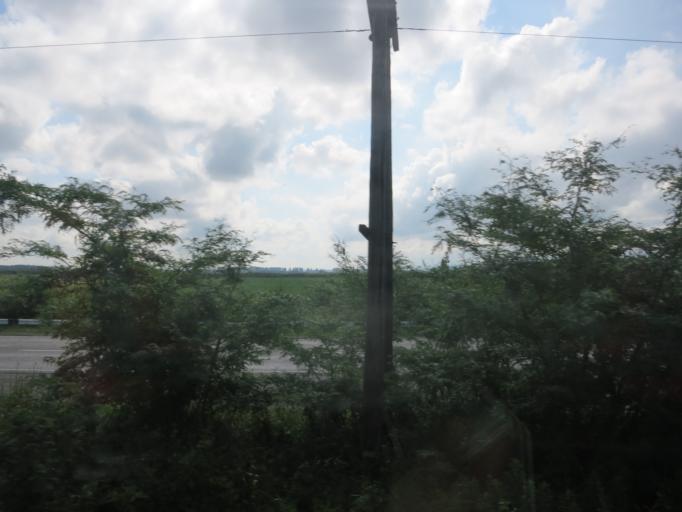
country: GE
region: Imereti
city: Samtredia
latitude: 42.1312
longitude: 42.3351
